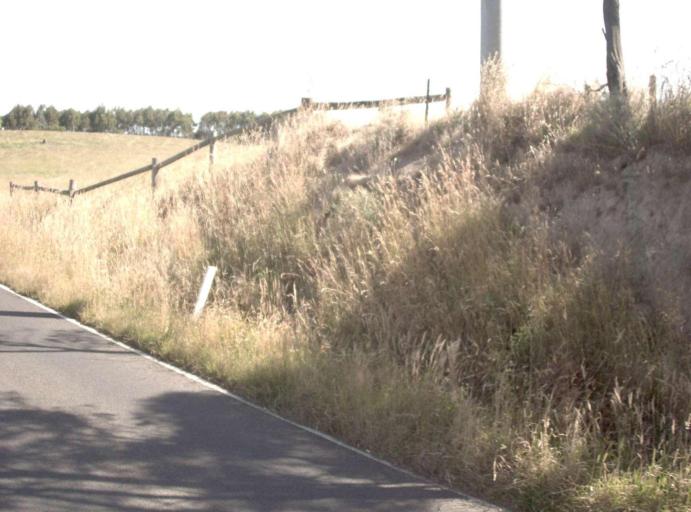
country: AU
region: Victoria
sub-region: Baw Baw
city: Warragul
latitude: -38.3517
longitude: 145.7835
